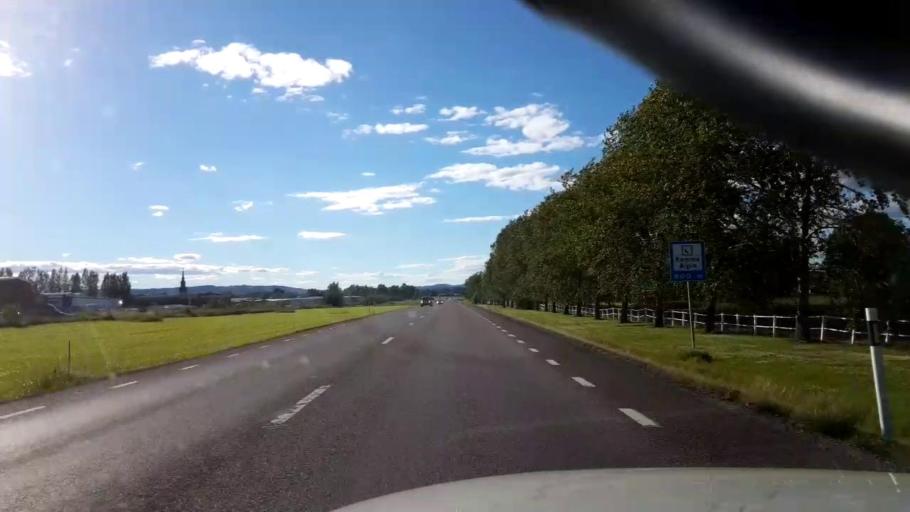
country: SE
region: Dalarna
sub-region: Borlange Kommun
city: Borlaenge
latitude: 60.4449
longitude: 15.4993
